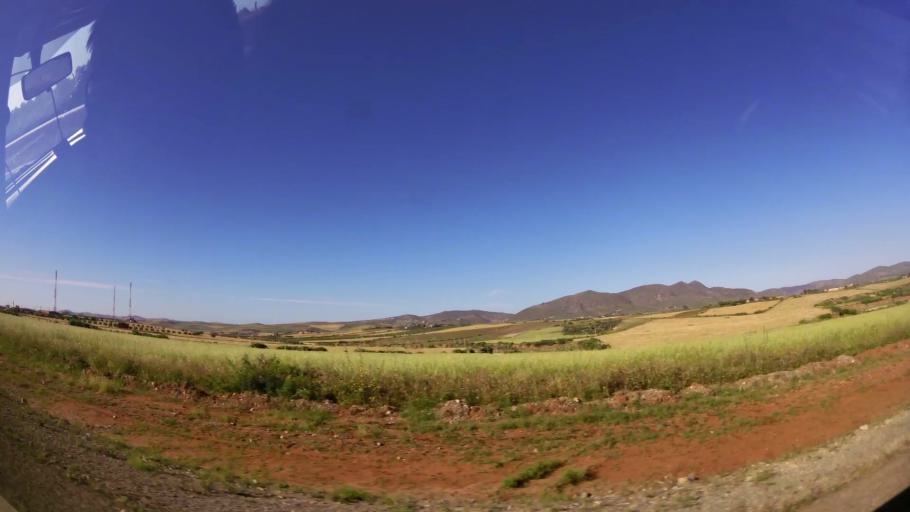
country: MA
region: Oriental
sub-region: Berkane-Taourirt
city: Ahfir
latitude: 34.9841
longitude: -2.1447
